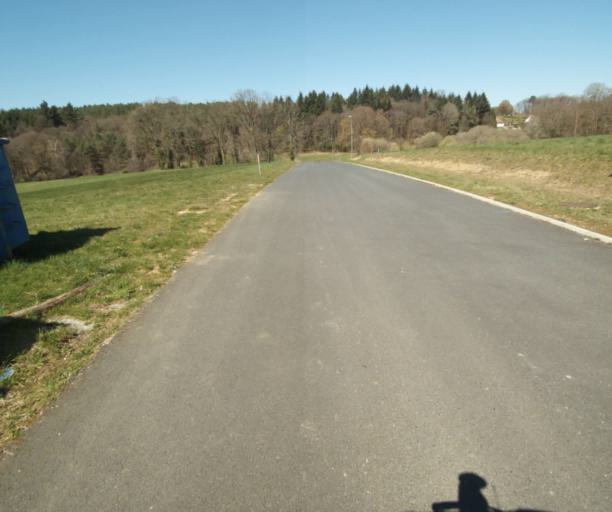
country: FR
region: Limousin
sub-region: Departement de la Correze
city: Saint-Mexant
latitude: 45.2714
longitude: 1.6618
